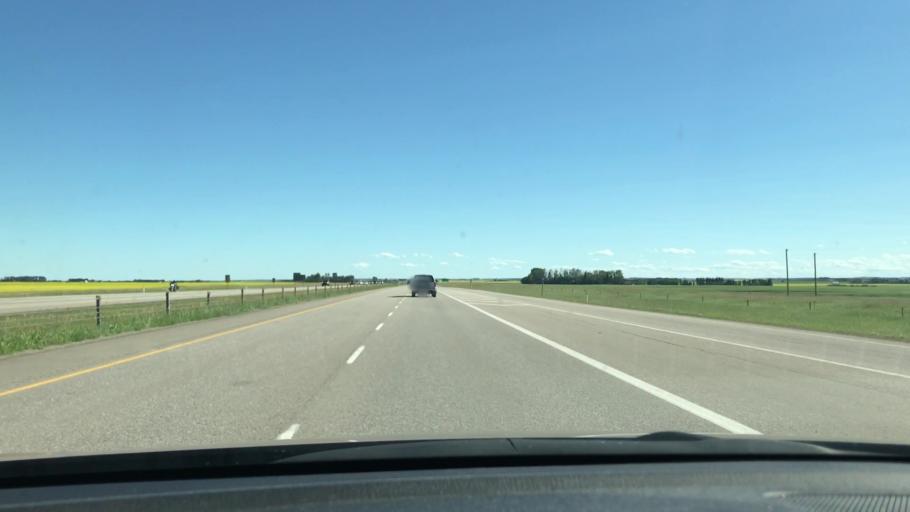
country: CA
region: Alberta
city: Didsbury
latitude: 51.6600
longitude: -114.0257
